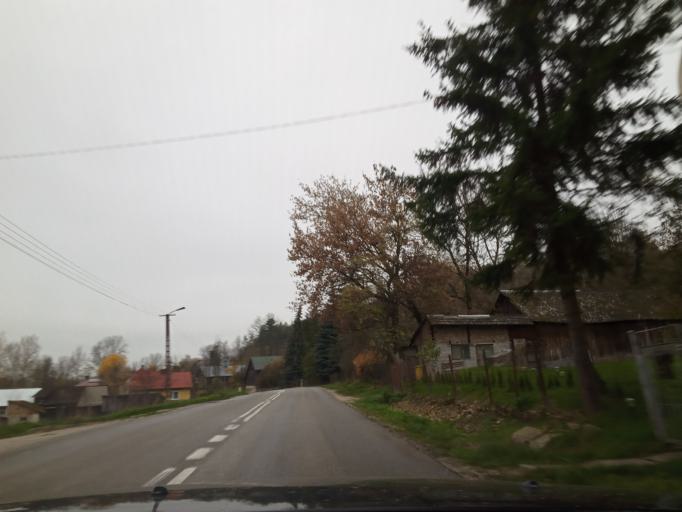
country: PL
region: Swietokrzyskie
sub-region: Powiat pinczowski
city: Dzialoszyce
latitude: 50.3789
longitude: 20.3369
